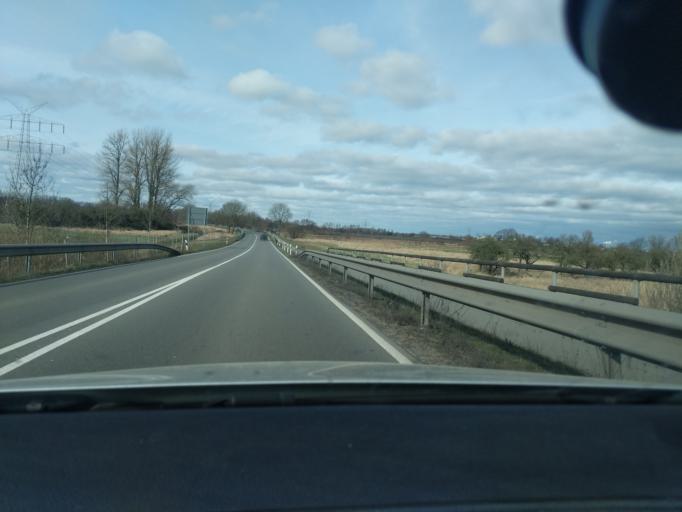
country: DE
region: Lower Saxony
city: Agathenburg
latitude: 53.5814
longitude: 9.5171
